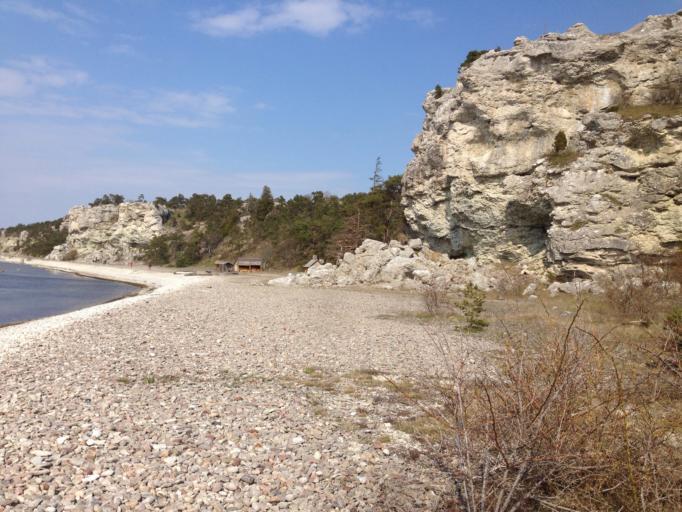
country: SE
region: Gotland
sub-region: Gotland
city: Slite
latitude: 57.8552
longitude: 18.6161
